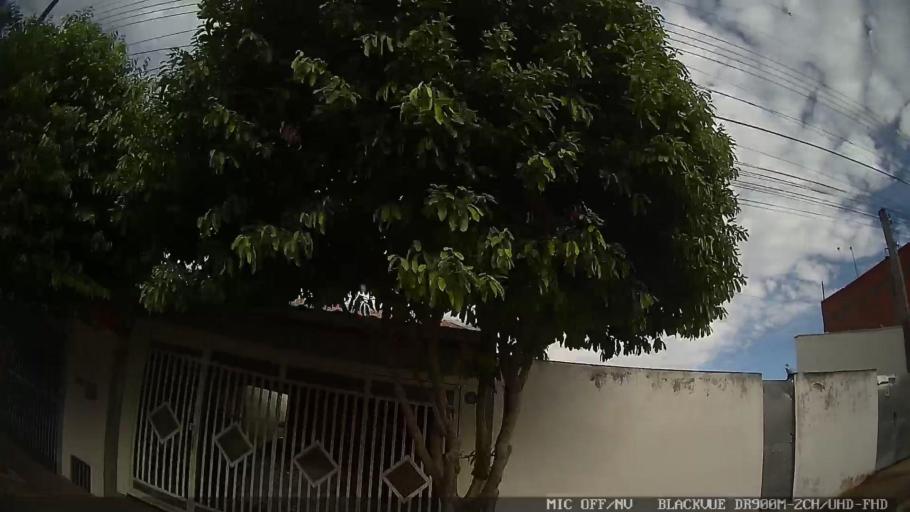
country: BR
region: Sao Paulo
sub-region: Salto
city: Salto
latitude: -23.1866
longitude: -47.2716
